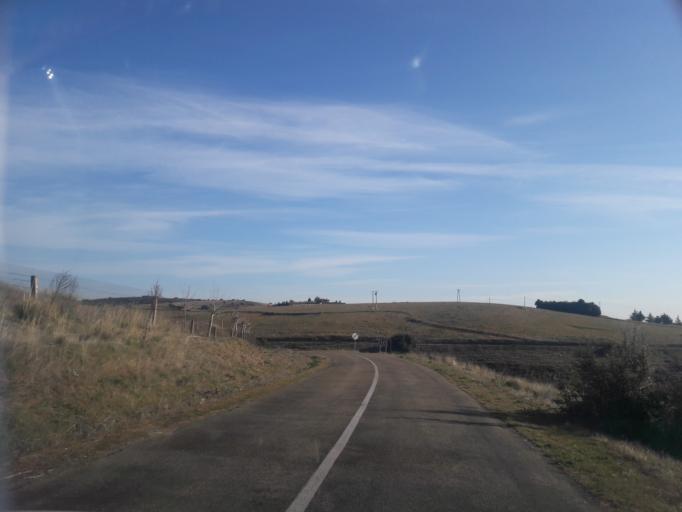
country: ES
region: Castille and Leon
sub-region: Provincia de Salamanca
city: Salvatierra de Tormes
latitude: 40.5873
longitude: -5.6042
